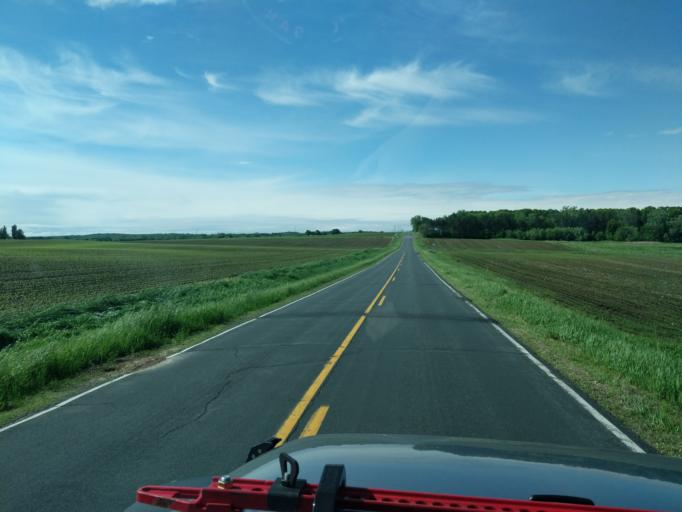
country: US
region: Wisconsin
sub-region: Saint Croix County
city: Hammond
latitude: 44.8737
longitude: -92.4969
